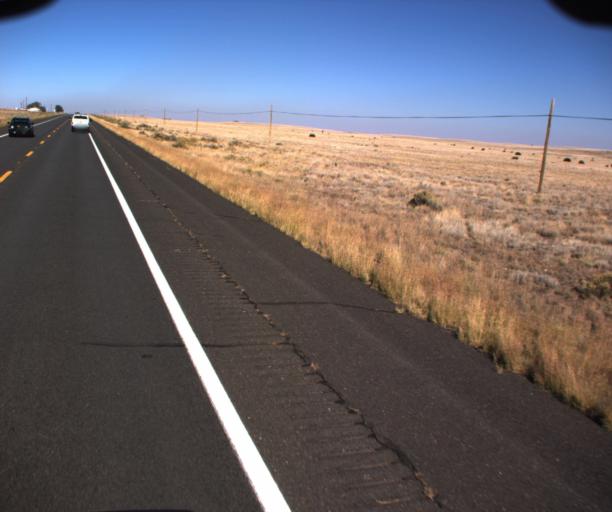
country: US
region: Arizona
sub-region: Coconino County
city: Flagstaff
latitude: 35.5862
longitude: -111.5286
